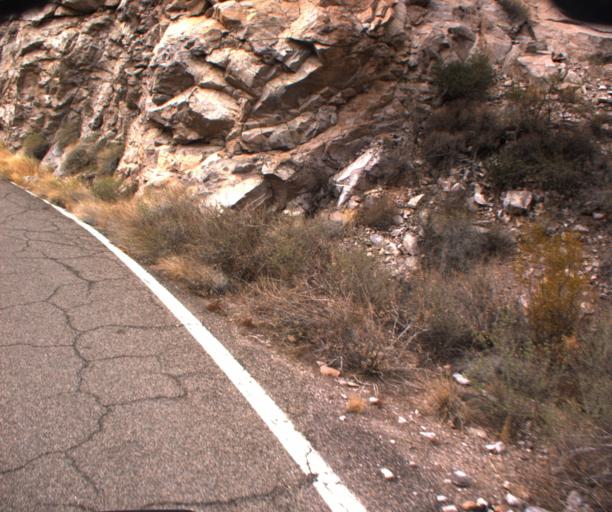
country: US
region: Arizona
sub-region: Pinal County
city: Apache Junction
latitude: 33.5324
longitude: -111.3793
